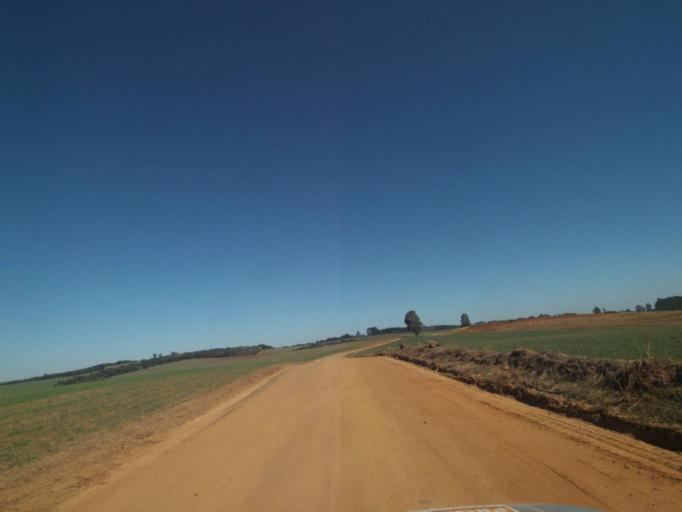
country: BR
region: Parana
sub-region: Tibagi
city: Tibagi
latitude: -24.5602
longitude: -50.6222
